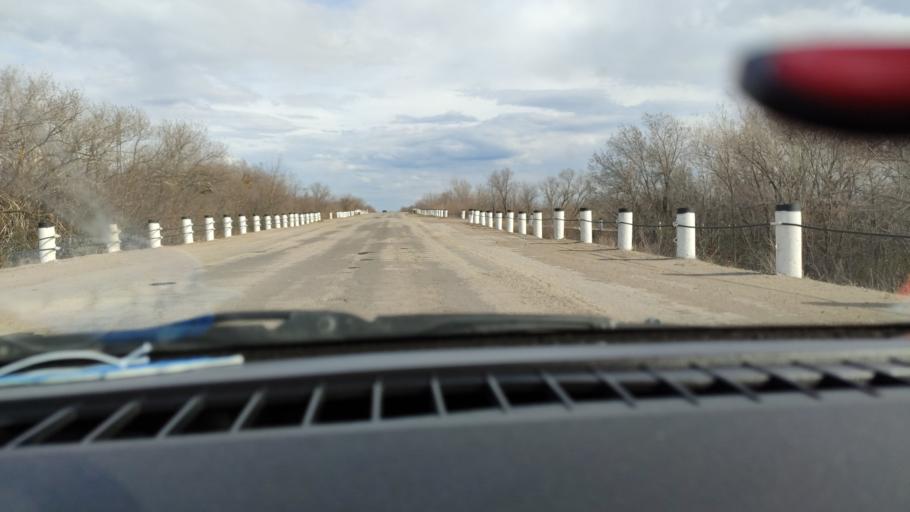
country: RU
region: Saratov
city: Krasnoarmeysk
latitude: 51.0719
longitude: 45.9855
